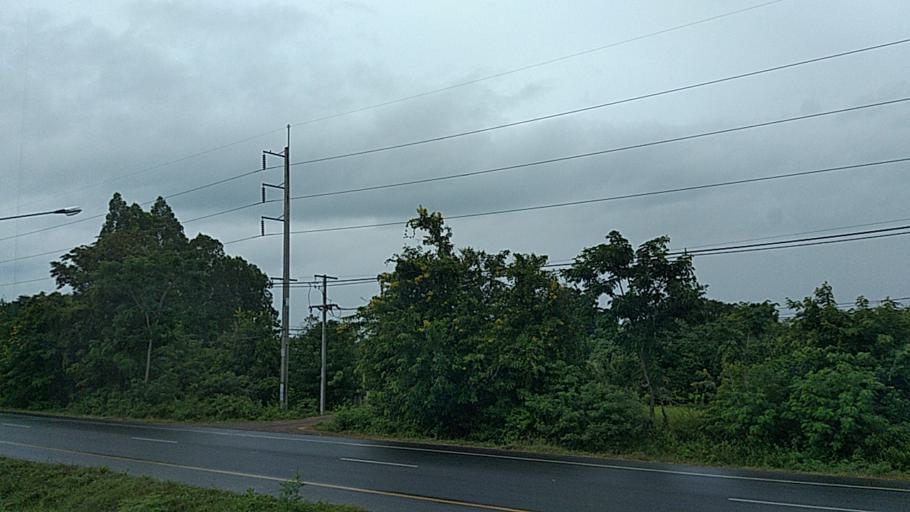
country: TH
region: Maha Sarakham
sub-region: Amphoe Borabue
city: Borabue
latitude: 16.0715
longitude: 103.1500
